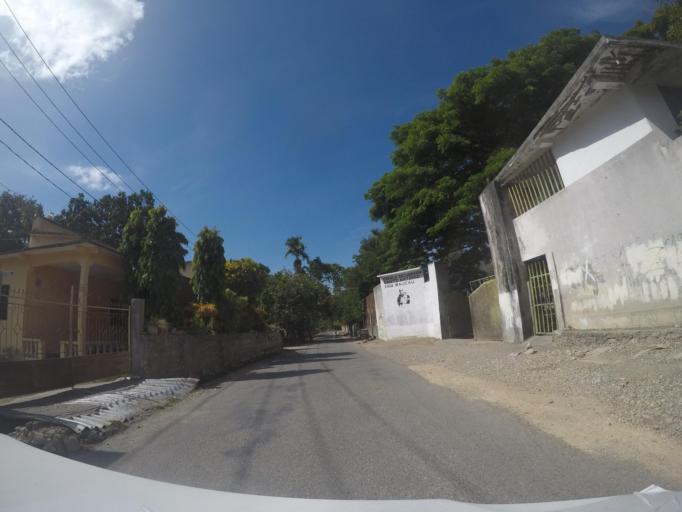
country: TL
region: Baucau
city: Baucau
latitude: -8.4591
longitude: 126.4551
